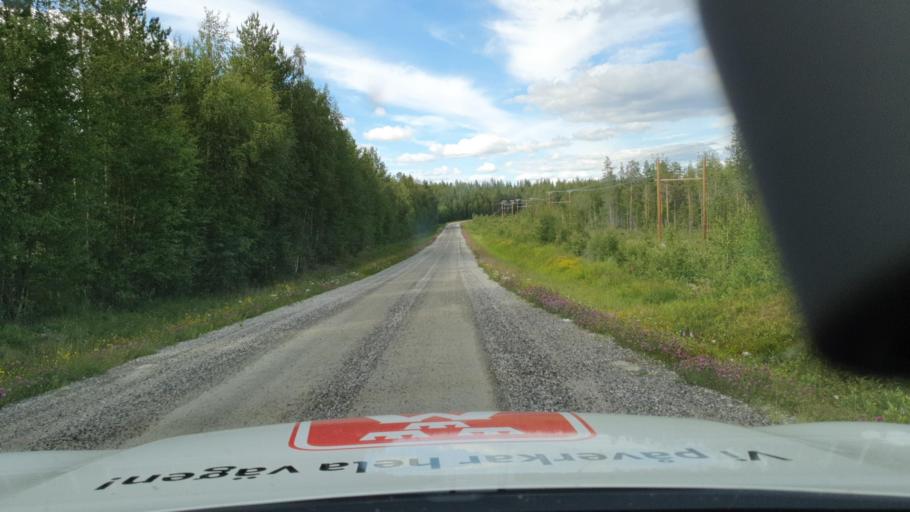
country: SE
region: Vaesterbotten
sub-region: Asele Kommun
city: Insjon
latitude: 64.2134
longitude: 17.8124
